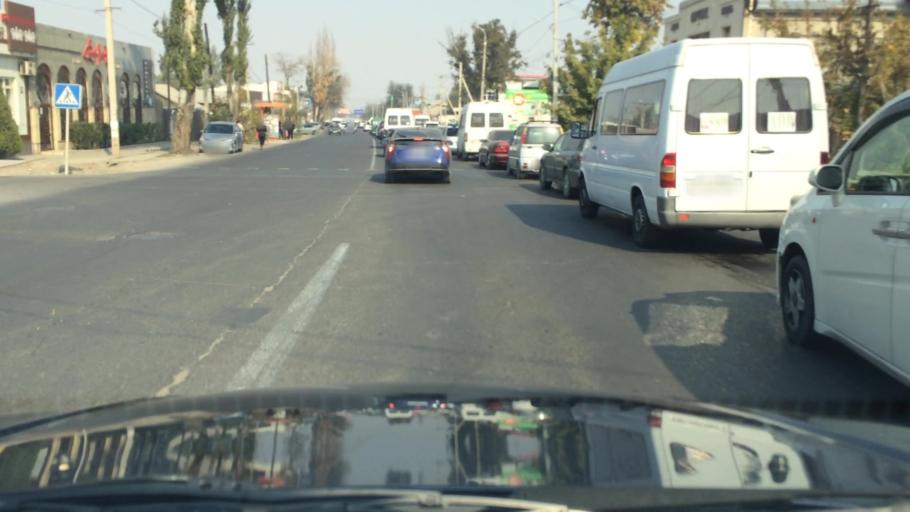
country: KG
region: Chuy
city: Lebedinovka
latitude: 42.8779
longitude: 74.6377
